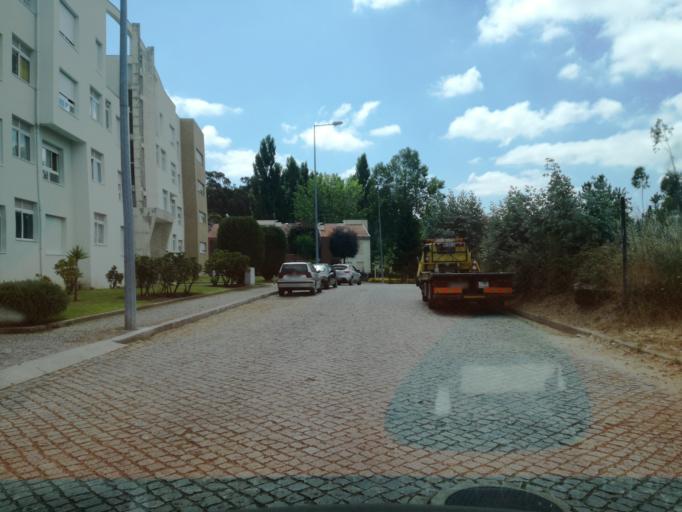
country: PT
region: Porto
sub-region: Maia
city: Nogueira
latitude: 41.2452
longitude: -8.5974
